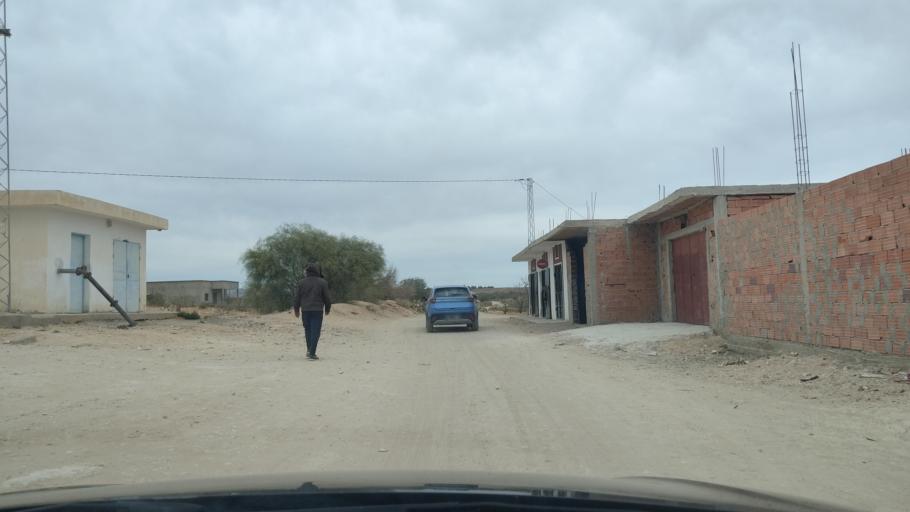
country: TN
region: Al Qasrayn
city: Kasserine
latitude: 35.2306
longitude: 8.9097
